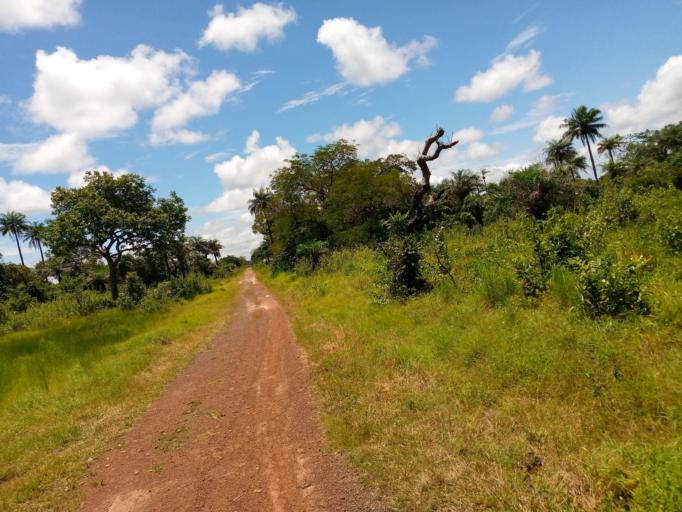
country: SL
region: Northern Province
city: Binkolo
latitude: 9.0747
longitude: -12.1456
